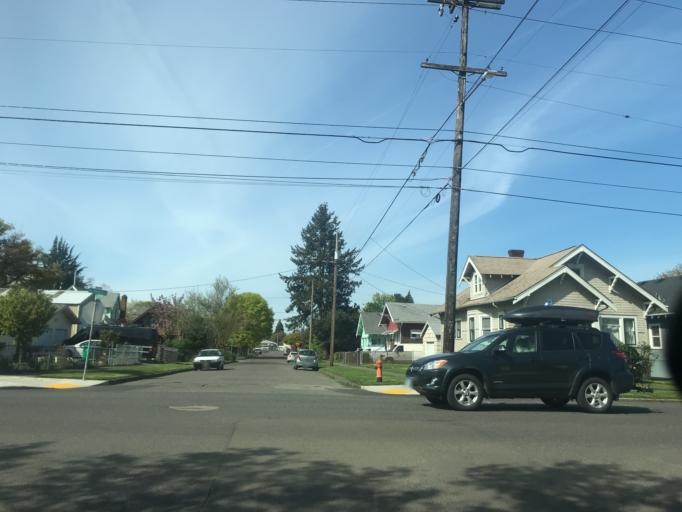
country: US
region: Oregon
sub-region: Multnomah County
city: Lents
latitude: 45.4830
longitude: -122.5867
